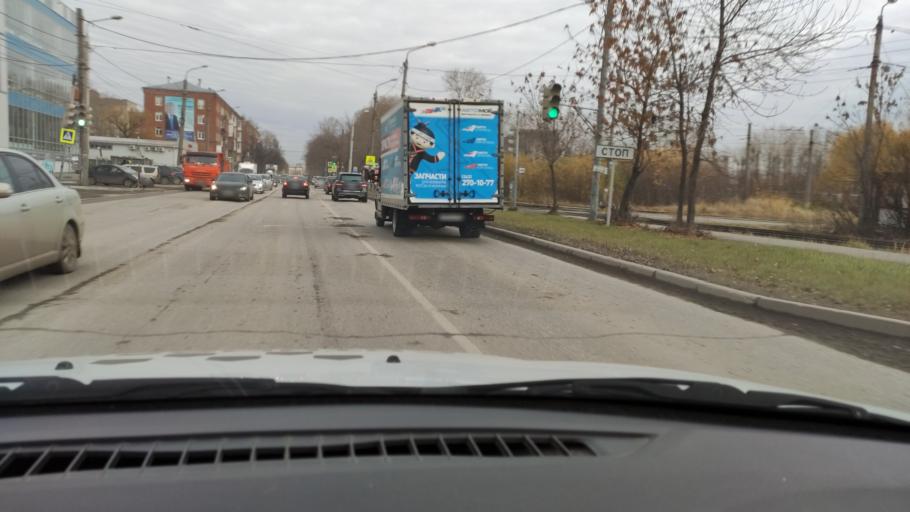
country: RU
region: Perm
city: Perm
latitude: 57.9646
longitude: 56.2444
